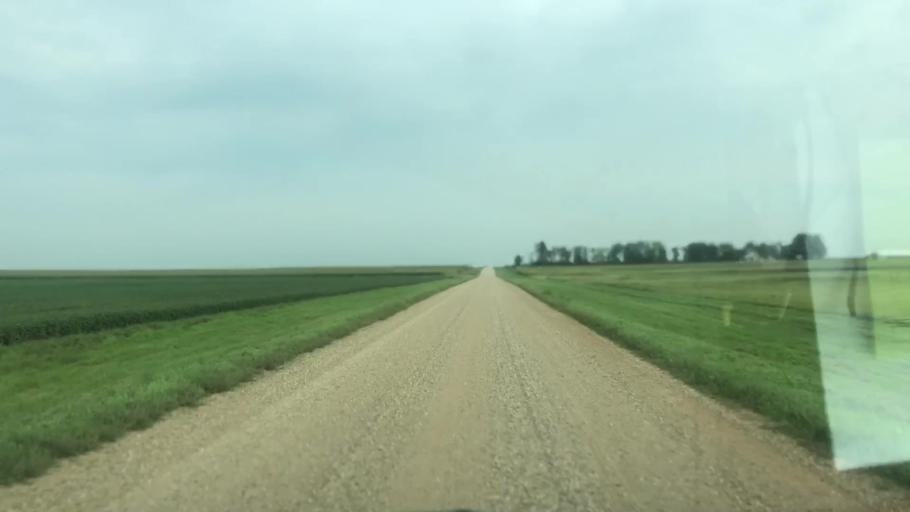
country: US
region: Iowa
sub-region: O'Brien County
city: Sheldon
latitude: 43.2685
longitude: -95.8618
